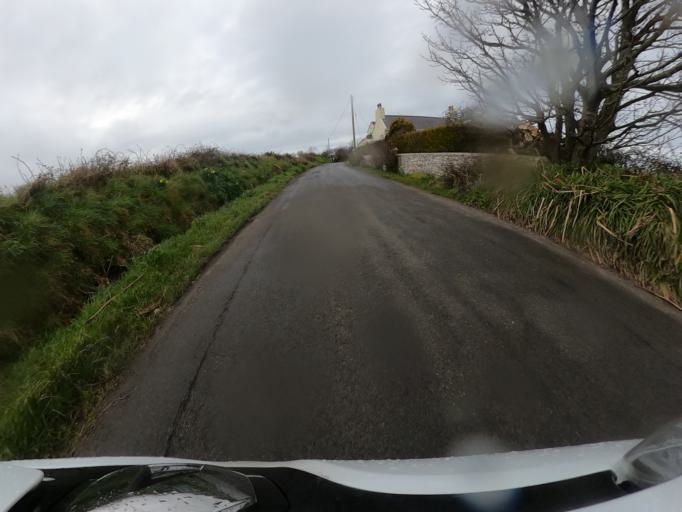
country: IM
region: Ramsey
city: Ramsey
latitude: 54.3735
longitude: -4.4504
